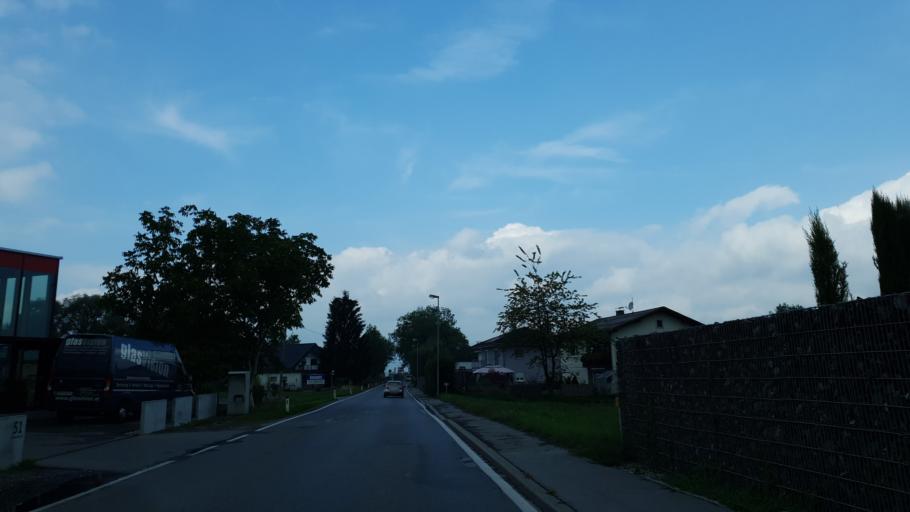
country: AT
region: Vorarlberg
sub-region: Politischer Bezirk Dornbirn
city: Dornbirn
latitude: 47.3987
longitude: 9.7199
